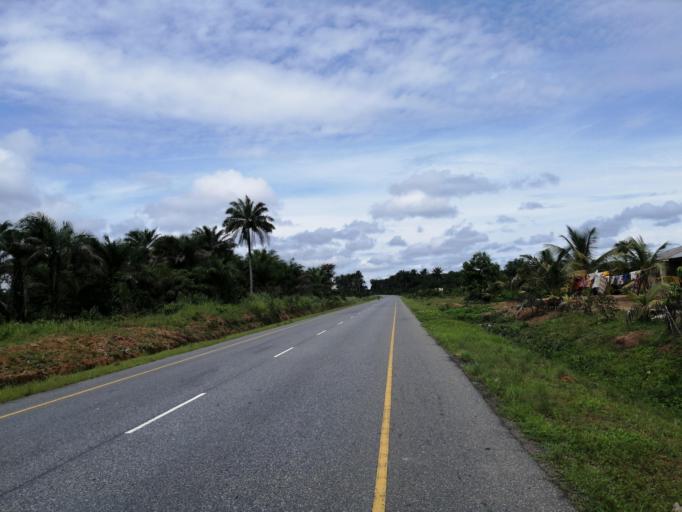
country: SL
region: Northern Province
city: Pepel
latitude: 8.7225
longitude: -12.9572
